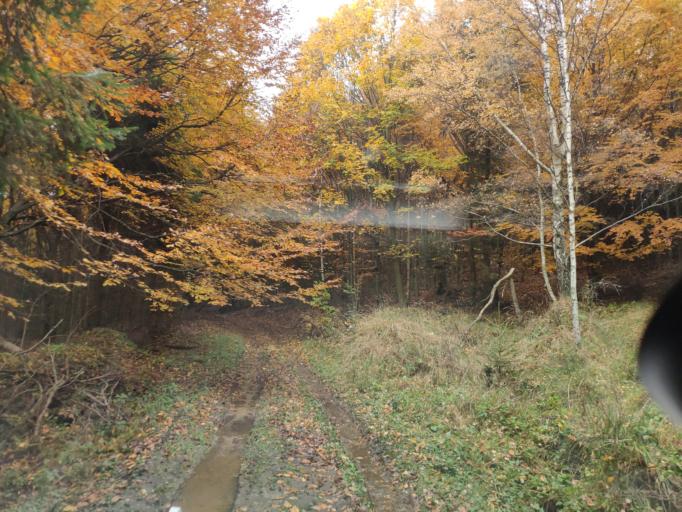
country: SK
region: Kosicky
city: Medzev
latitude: 48.7501
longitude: 20.9823
